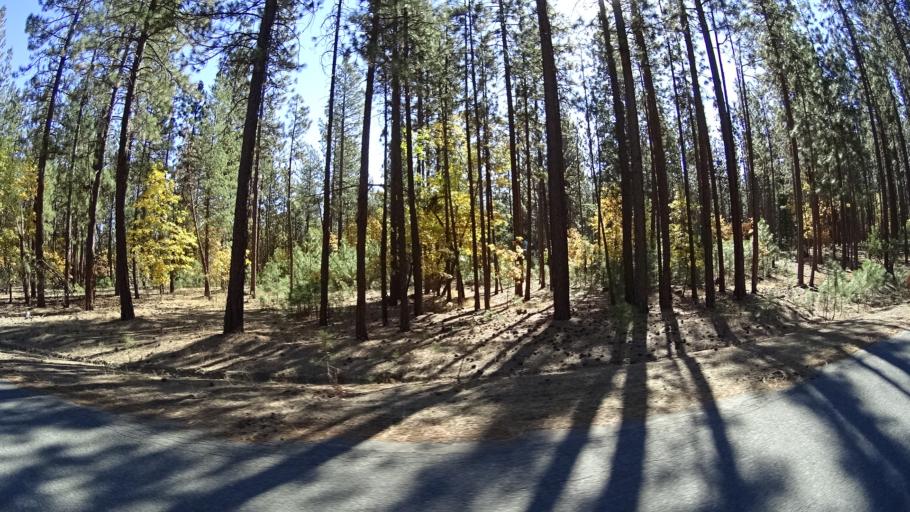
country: US
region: California
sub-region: Siskiyou County
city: Yreka
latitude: 41.5128
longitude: -122.9091
